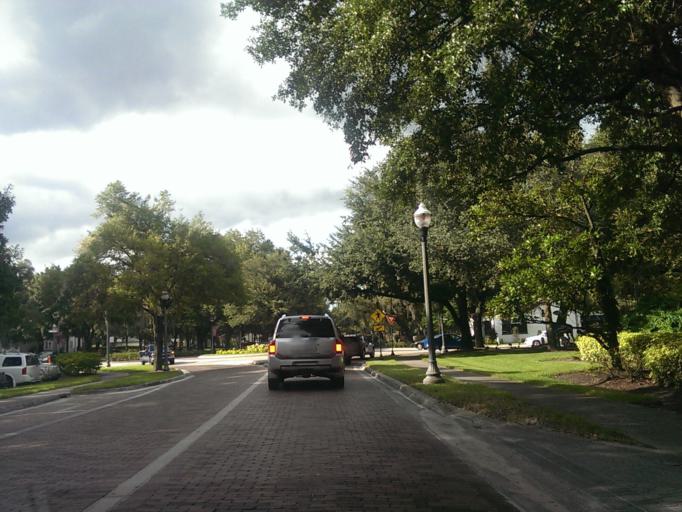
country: US
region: Florida
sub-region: Orange County
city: Windermere
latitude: 28.4940
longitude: -81.5343
